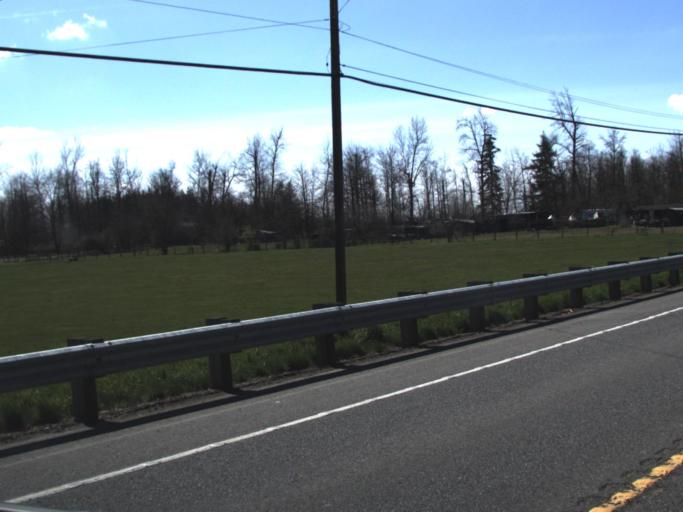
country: US
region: Washington
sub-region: Pierce County
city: Buckley
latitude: 47.2102
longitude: -122.0451
